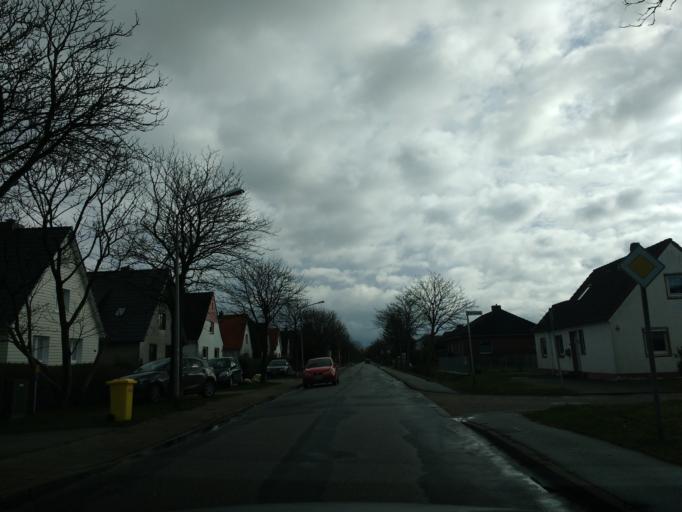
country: DE
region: Lower Saxony
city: Cuxhaven
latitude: 53.8489
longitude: 8.6793
